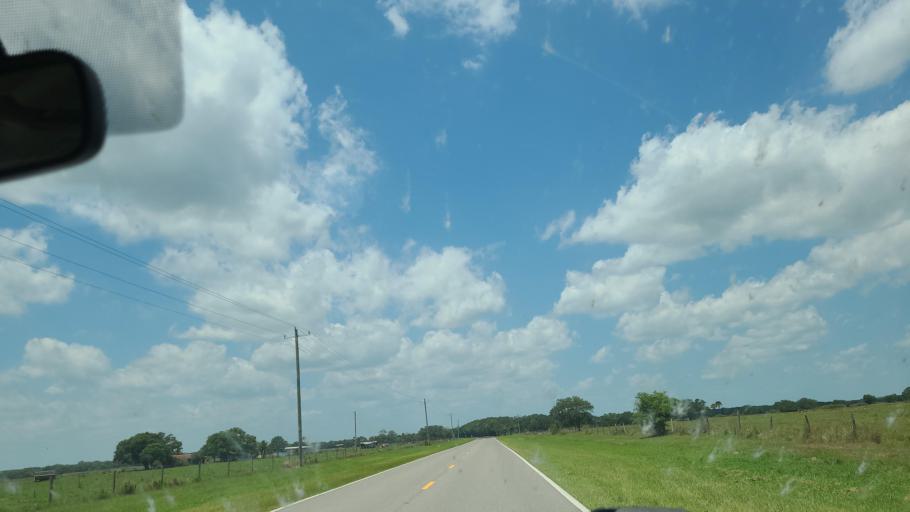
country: US
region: Florida
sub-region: Okeechobee County
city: Cypress Quarters
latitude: 27.3937
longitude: -80.8823
